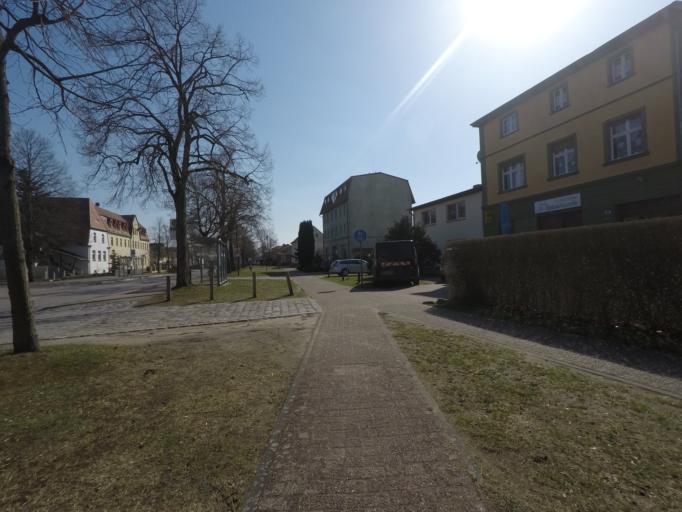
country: DE
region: Brandenburg
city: Britz
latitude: 52.8668
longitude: 13.7489
